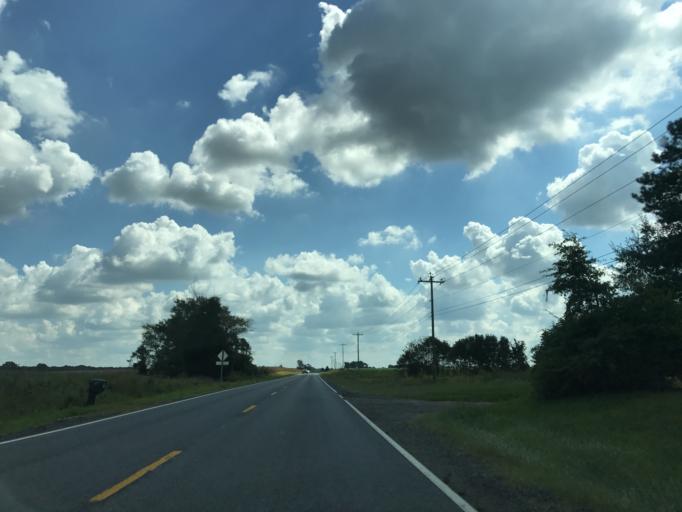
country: US
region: Maryland
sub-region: Queen Anne's County
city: Centreville
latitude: 39.0199
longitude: -76.0085
